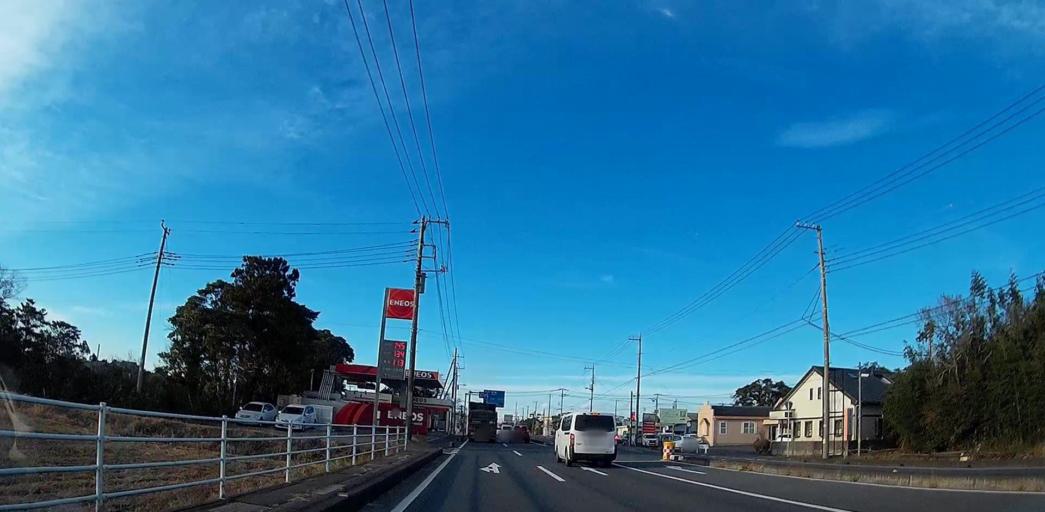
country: JP
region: Chiba
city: Omigawa
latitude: 35.8286
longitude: 140.7224
